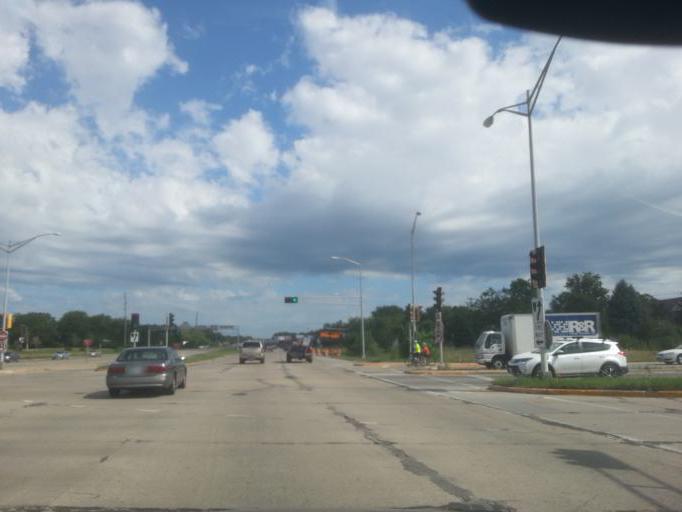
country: US
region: Wisconsin
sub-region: Dane County
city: Monona
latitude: 43.0477
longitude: -89.3077
